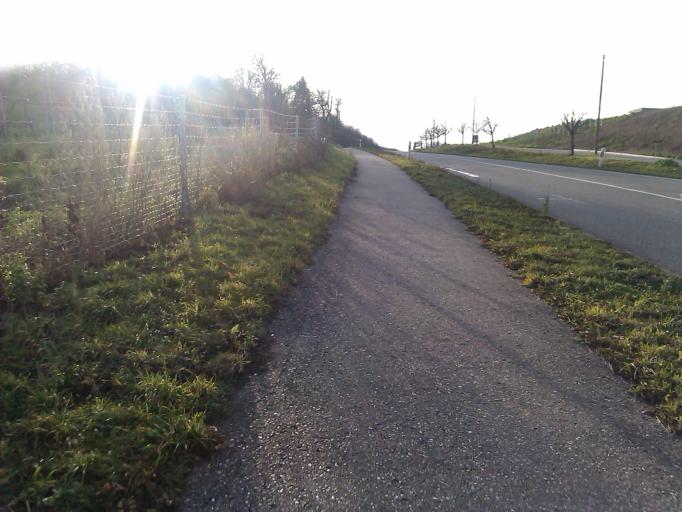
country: DE
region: Baden-Wuerttemberg
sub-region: Regierungsbezirk Stuttgart
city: Erlenbach
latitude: 49.1671
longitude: 9.2433
